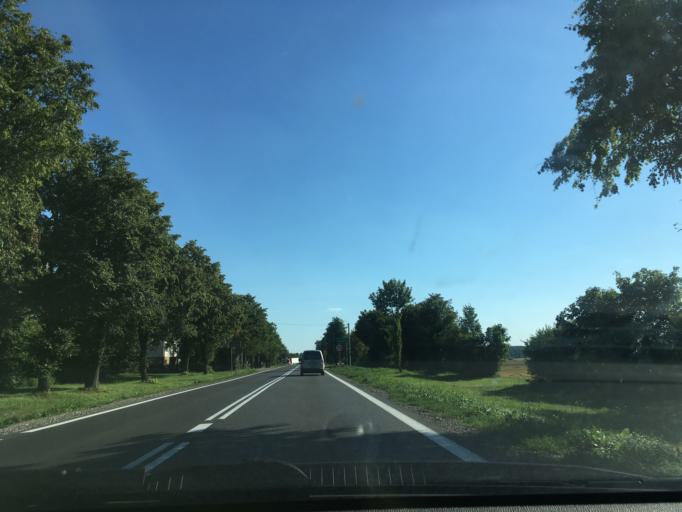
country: PL
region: Podlasie
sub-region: Powiat sokolski
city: Suchowola
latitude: 53.4739
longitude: 23.0910
